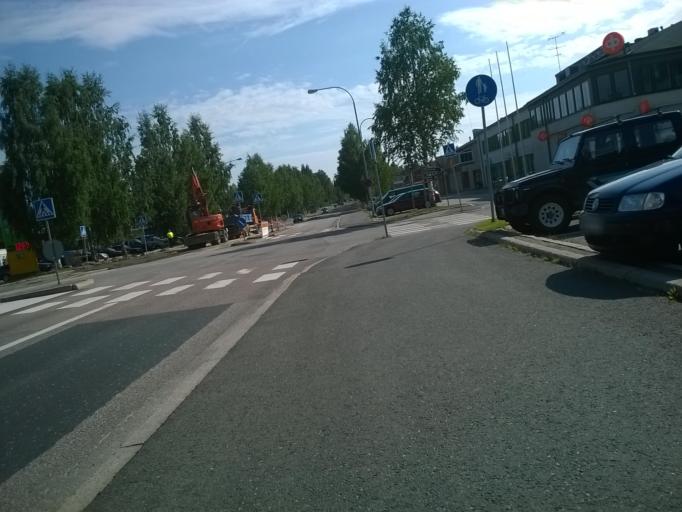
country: FI
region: Kainuu
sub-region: Kehys-Kainuu
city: Kuhmo
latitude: 64.1275
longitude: 29.5231
